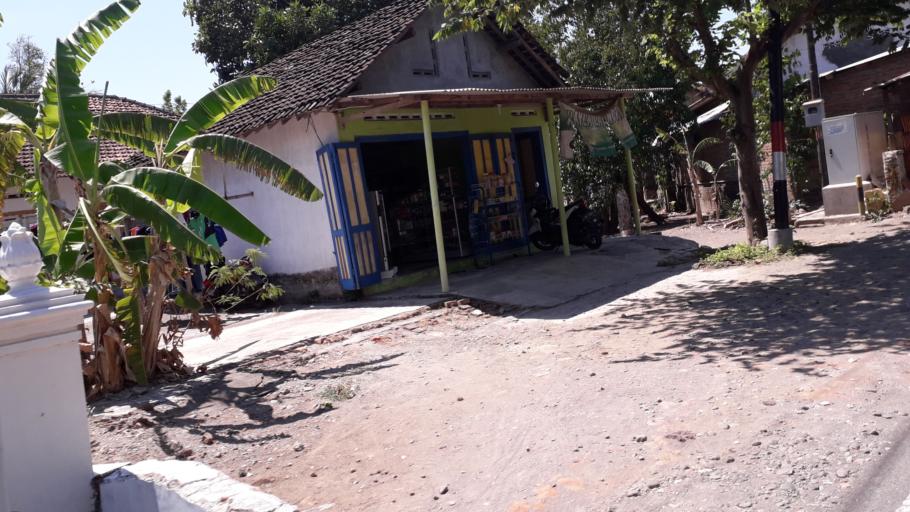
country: ID
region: Daerah Istimewa Yogyakarta
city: Pundong
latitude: -7.9830
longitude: 110.3163
